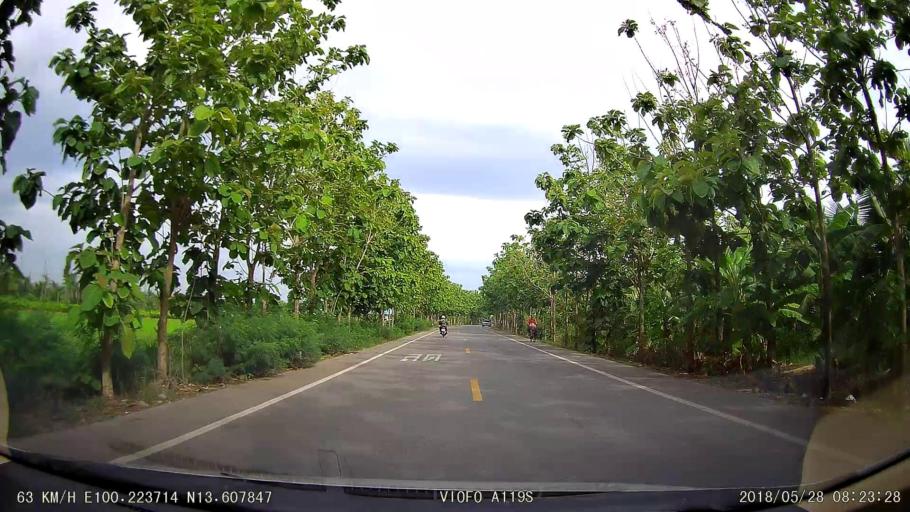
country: TH
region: Samut Sakhon
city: Krathum Baen
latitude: 13.6080
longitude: 100.2234
